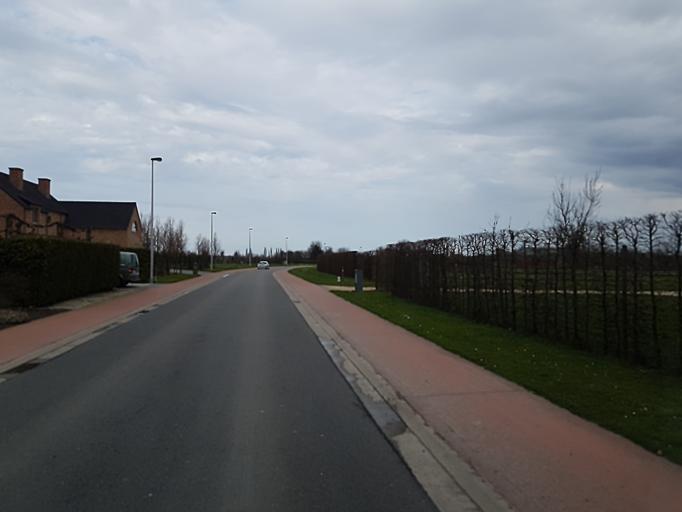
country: BE
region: Flanders
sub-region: Provincie Limburg
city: Nieuwerkerken
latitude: 50.9060
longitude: 5.2391
